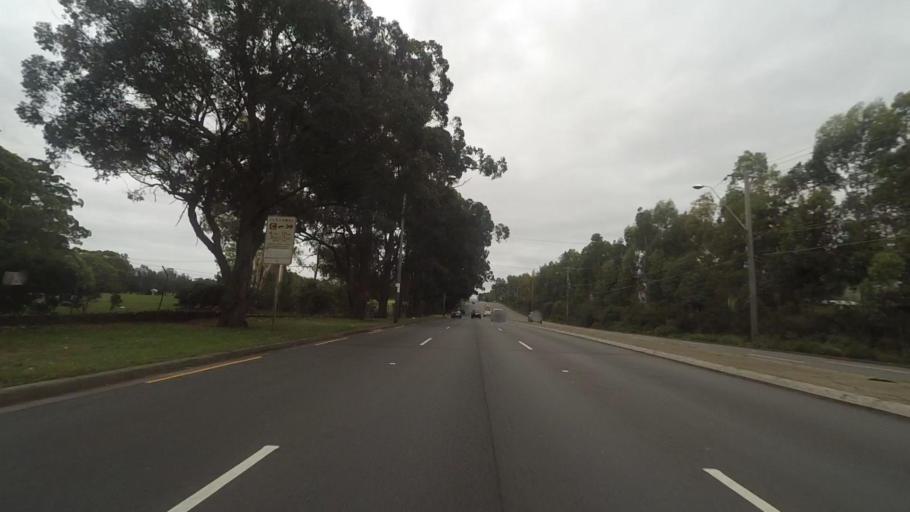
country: AU
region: New South Wales
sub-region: Auburn
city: Berala
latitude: -33.8810
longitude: 151.0406
